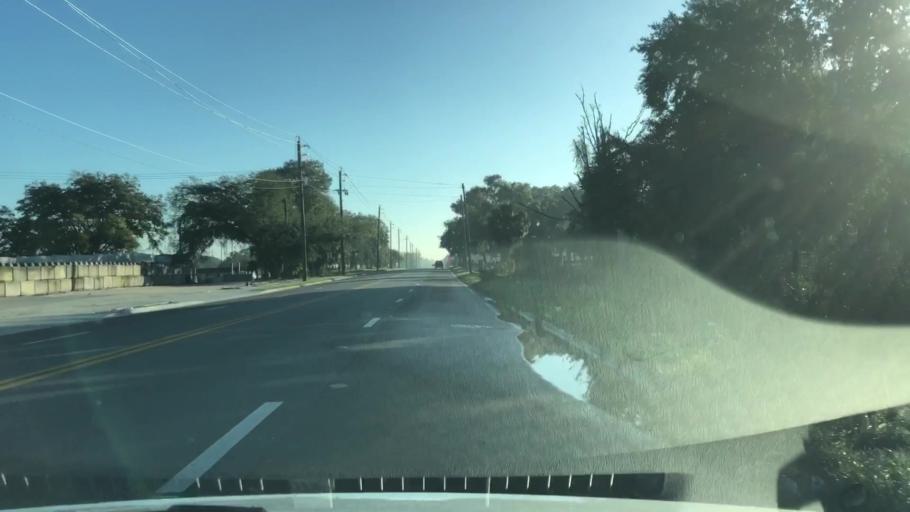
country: US
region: Florida
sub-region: Seminole County
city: Sanford
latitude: 28.7865
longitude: -81.2912
